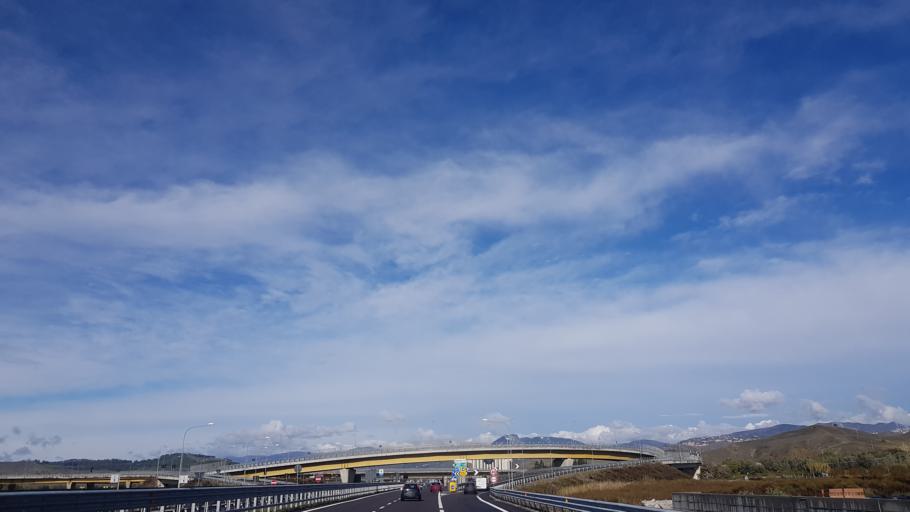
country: IT
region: Calabria
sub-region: Provincia di Catanzaro
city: Catanzaro
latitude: 38.8482
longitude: 16.5806
